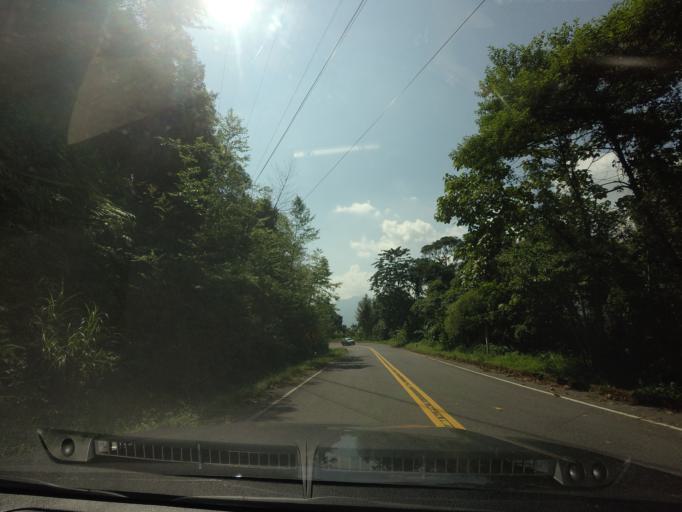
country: TH
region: Nan
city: Bo Kluea
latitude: 19.0418
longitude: 101.0887
